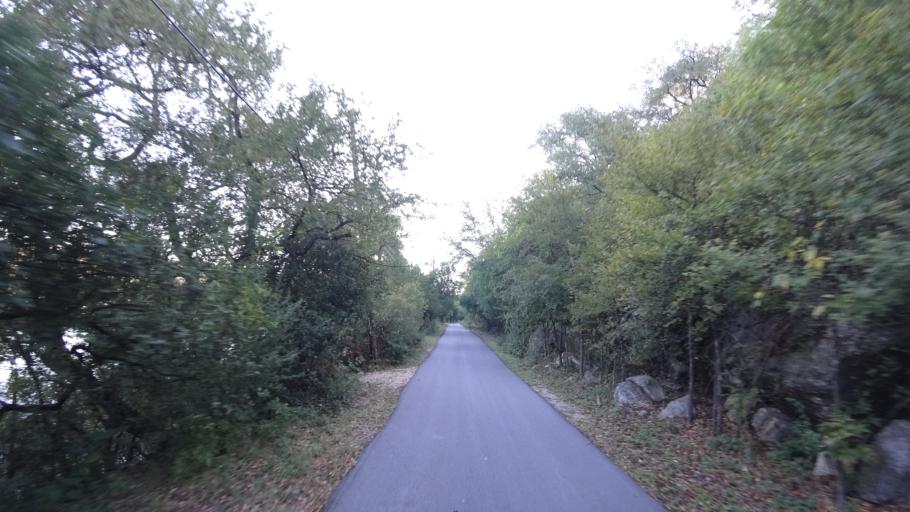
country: US
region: Texas
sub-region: Travis County
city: West Lake Hills
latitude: 30.3452
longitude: -97.8102
